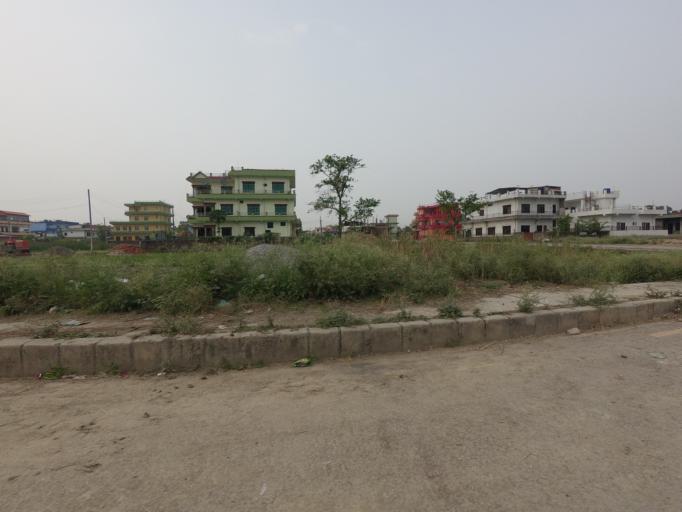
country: NP
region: Western Region
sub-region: Lumbini Zone
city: Bhairahawa
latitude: 27.5219
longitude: 83.4445
